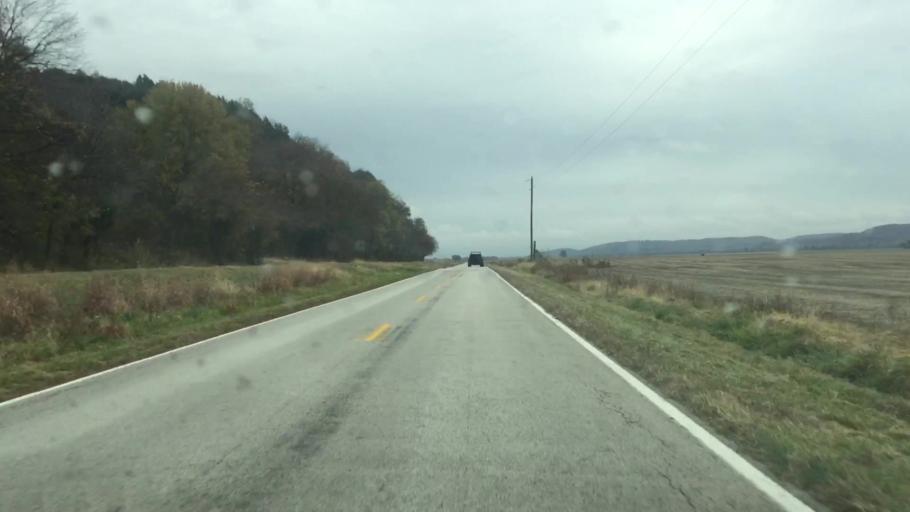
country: US
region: Missouri
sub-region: Gasconade County
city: Hermann
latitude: 38.7032
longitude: -91.5683
